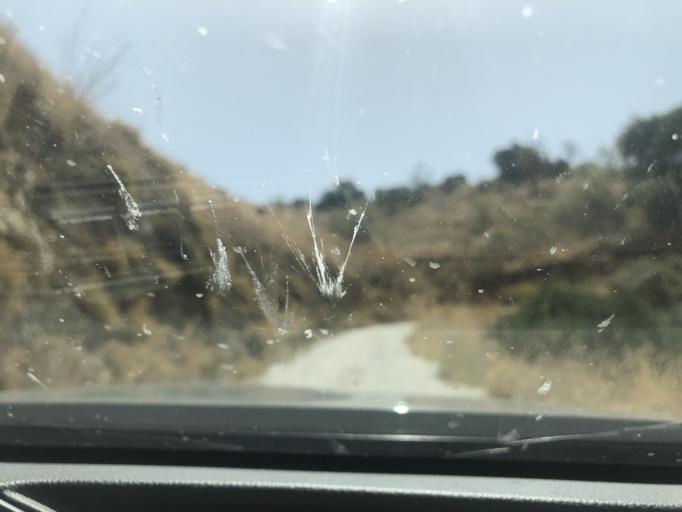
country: ES
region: Andalusia
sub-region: Provincia de Malaga
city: Cartama
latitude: 36.7081
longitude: -4.6247
